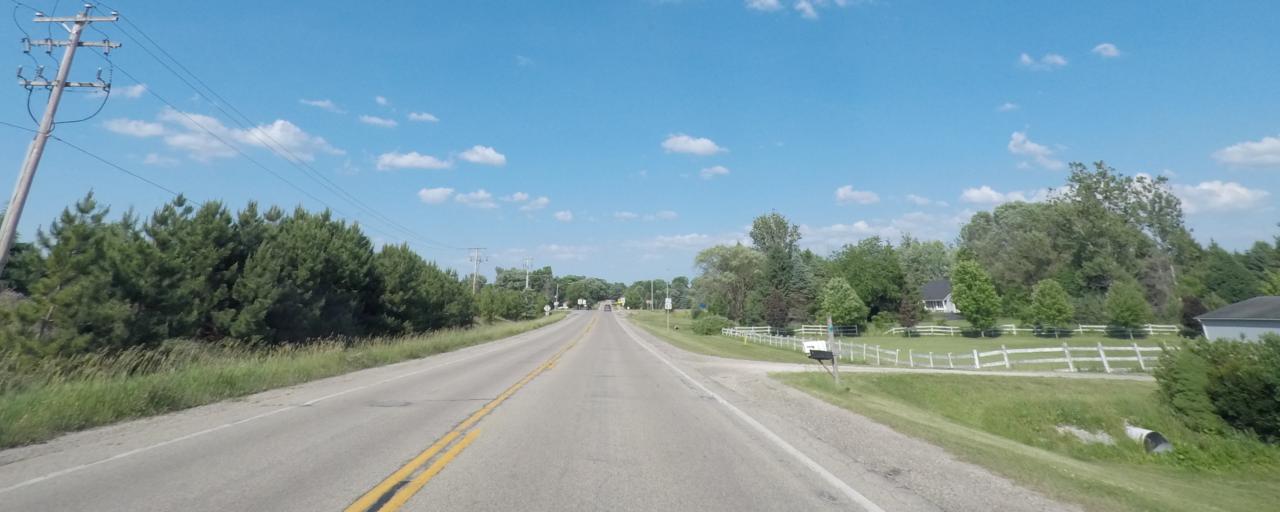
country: US
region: Wisconsin
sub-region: Walworth County
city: Potter Lake
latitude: 42.8292
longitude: -88.3041
